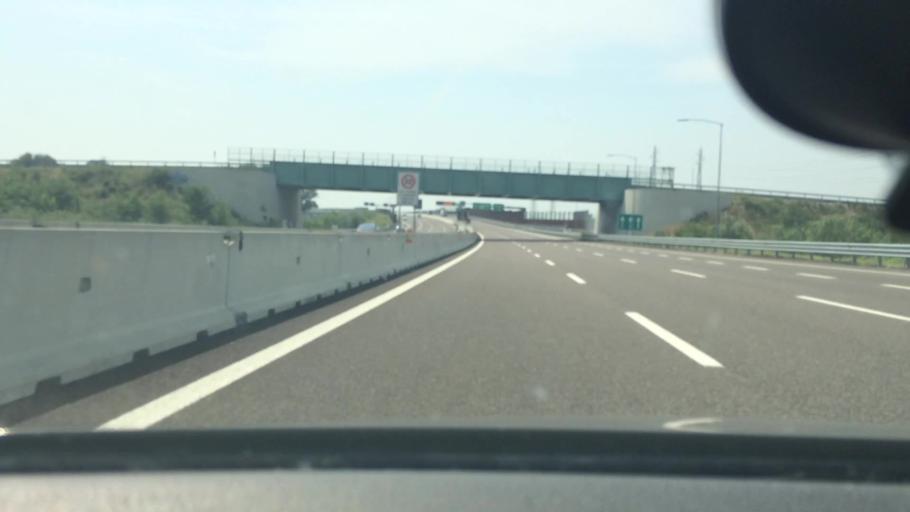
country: IT
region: Lombardy
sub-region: Citta metropolitana di Milano
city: Pozzuolo Martesana
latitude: 45.5132
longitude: 9.4404
